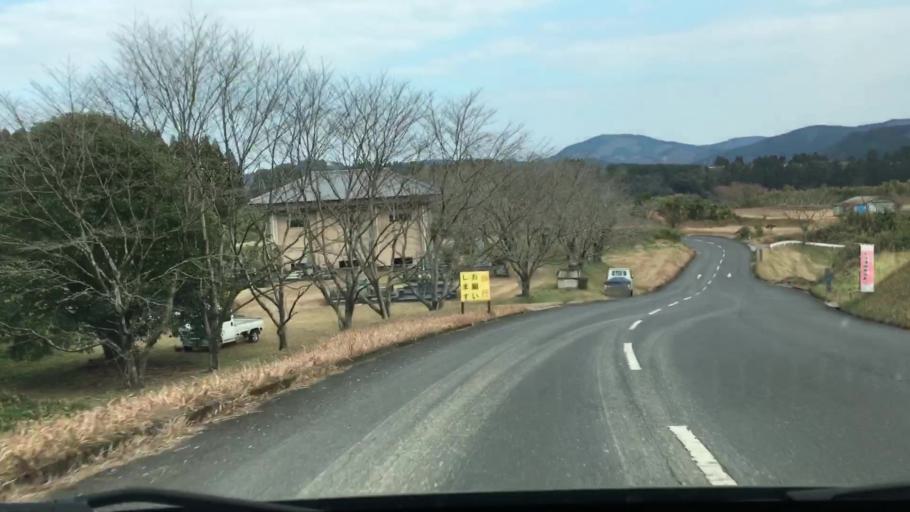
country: JP
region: Miyazaki
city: Kushima
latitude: 31.4964
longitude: 131.2342
